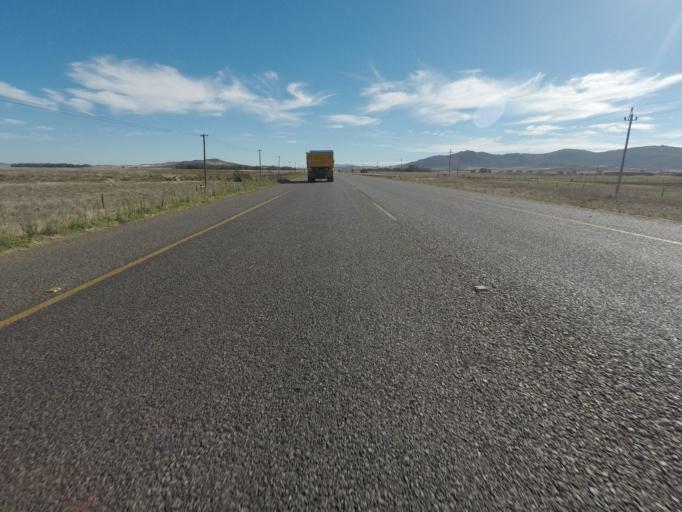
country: ZA
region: Western Cape
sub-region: West Coast District Municipality
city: Malmesbury
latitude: -33.6302
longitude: 18.7225
